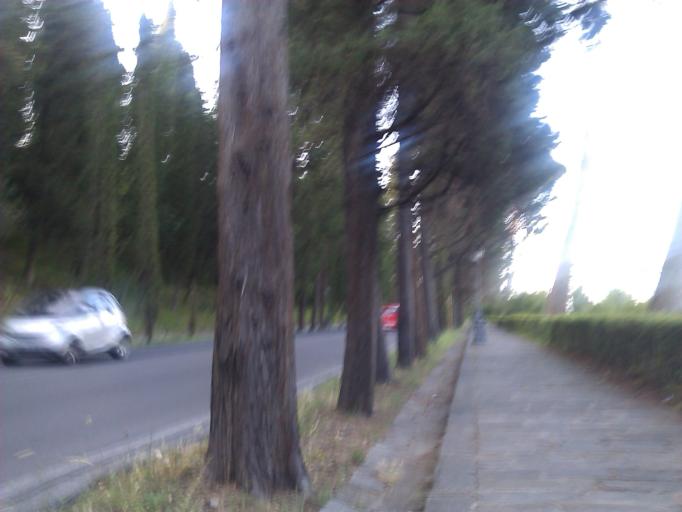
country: IT
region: Tuscany
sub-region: Province of Florence
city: Florence
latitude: 43.7589
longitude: 11.2693
